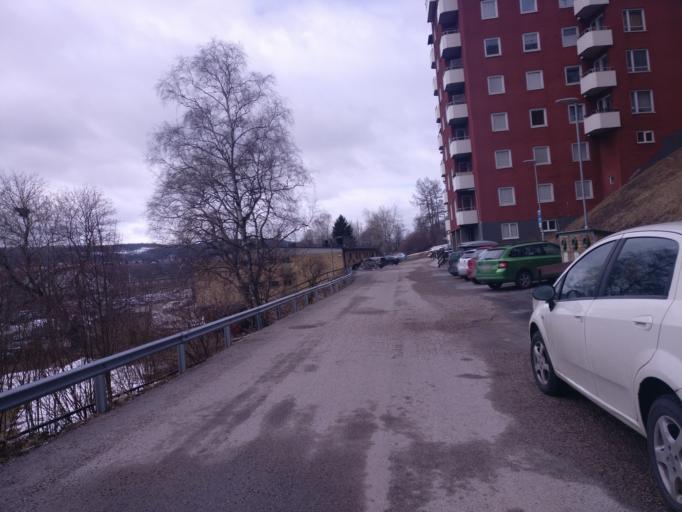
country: SE
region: Vaesternorrland
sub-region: Sundsvalls Kommun
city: Sundsvall
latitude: 62.3953
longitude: 17.2952
